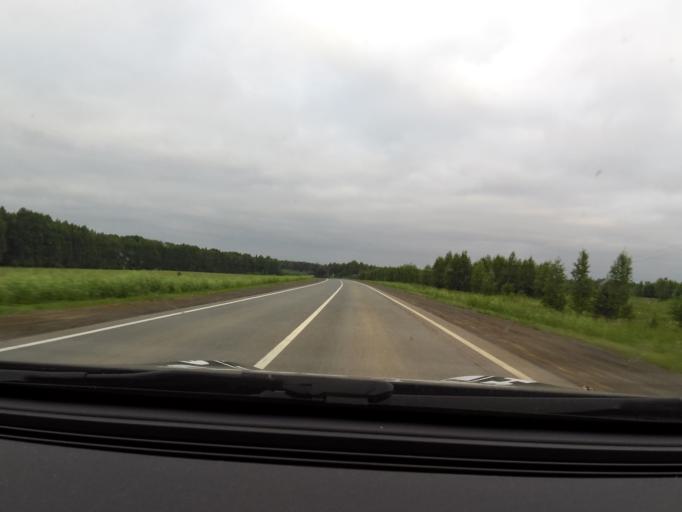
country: RU
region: Perm
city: Karagay
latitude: 58.2862
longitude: 54.8179
